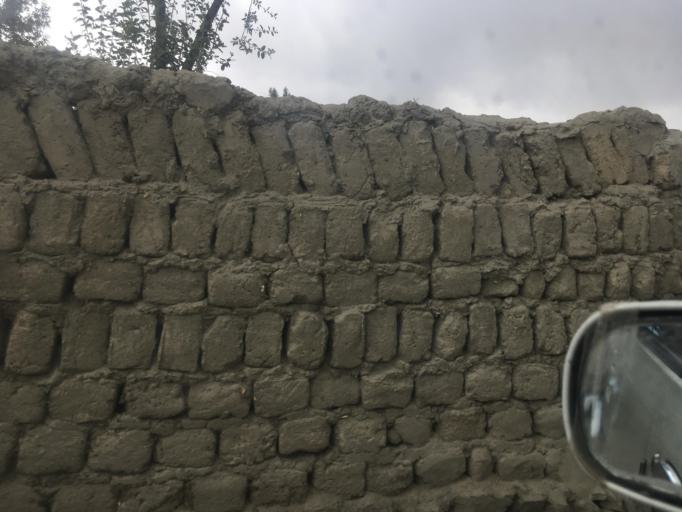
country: PK
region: Gilgit-Baltistan
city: Skardu
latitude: 35.3257
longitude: 75.5718
